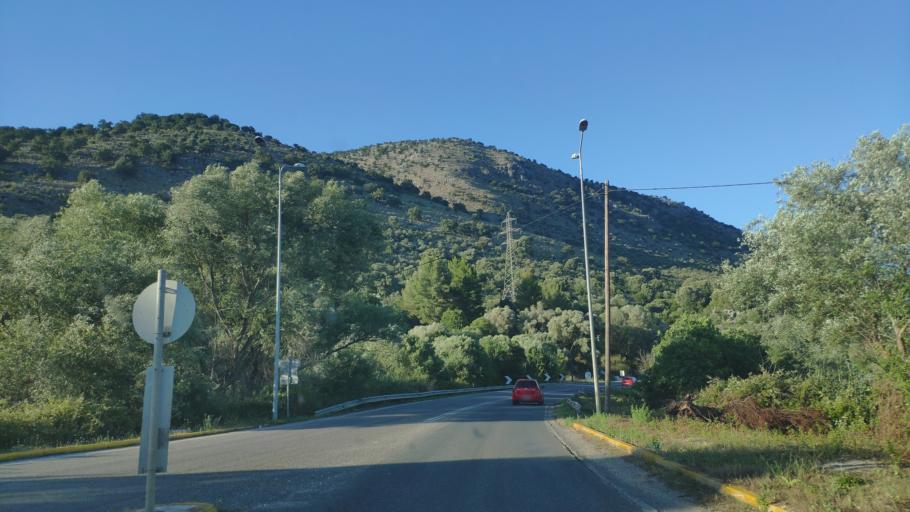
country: GR
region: Epirus
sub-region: Nomos Prevezis
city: Louros
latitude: 39.1749
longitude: 20.7646
